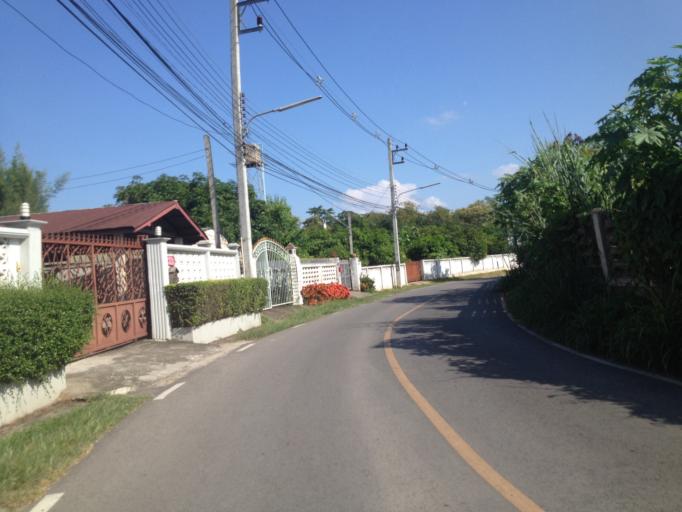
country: TH
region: Chiang Mai
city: Chiang Mai
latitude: 18.7526
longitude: 98.9347
